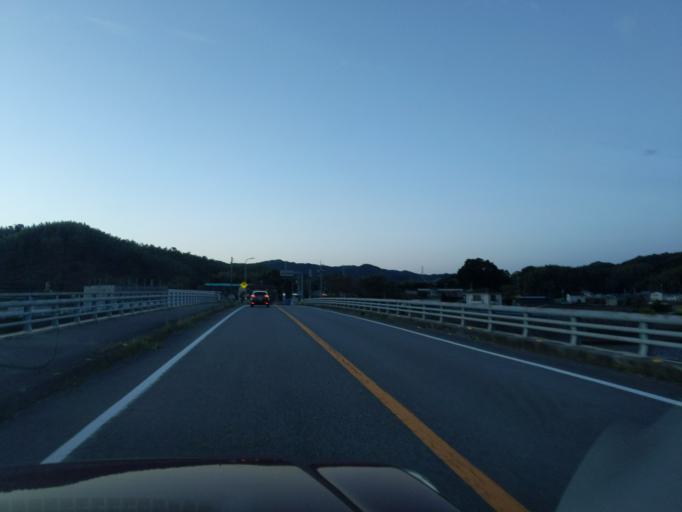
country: JP
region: Tokushima
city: Anan
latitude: 33.8493
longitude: 134.6260
